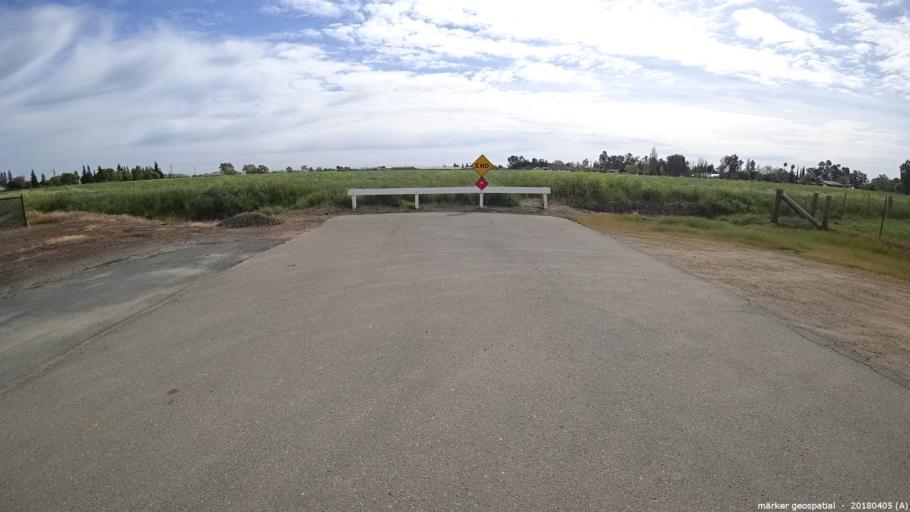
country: US
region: California
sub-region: Sacramento County
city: Galt
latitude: 38.2709
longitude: -121.3334
